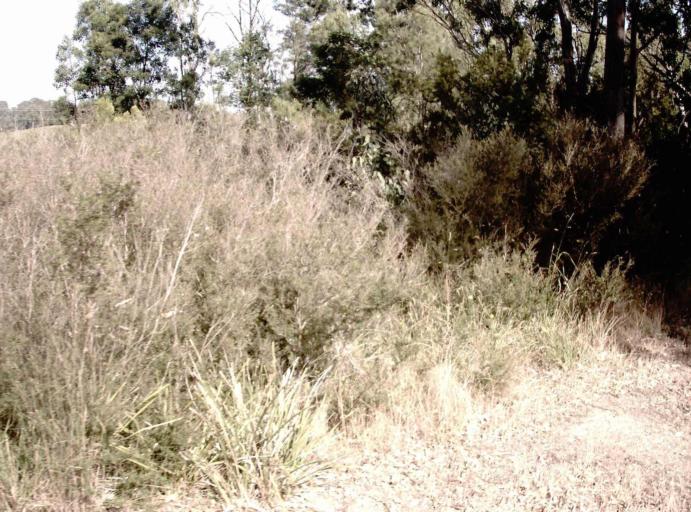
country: AU
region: Victoria
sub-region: East Gippsland
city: Lakes Entrance
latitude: -37.7884
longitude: 147.8295
